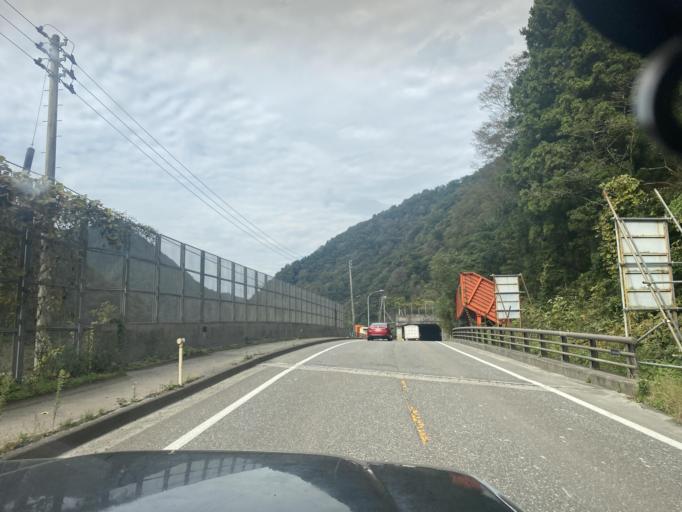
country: JP
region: Niigata
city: Itoigawa
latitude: 36.9414
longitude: 137.8567
